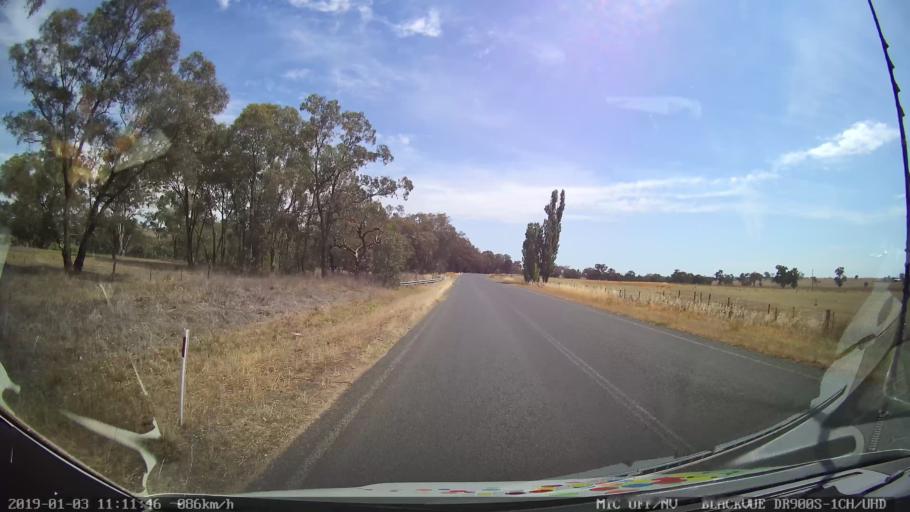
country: AU
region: New South Wales
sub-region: Young
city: Young
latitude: -34.2102
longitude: 148.2604
